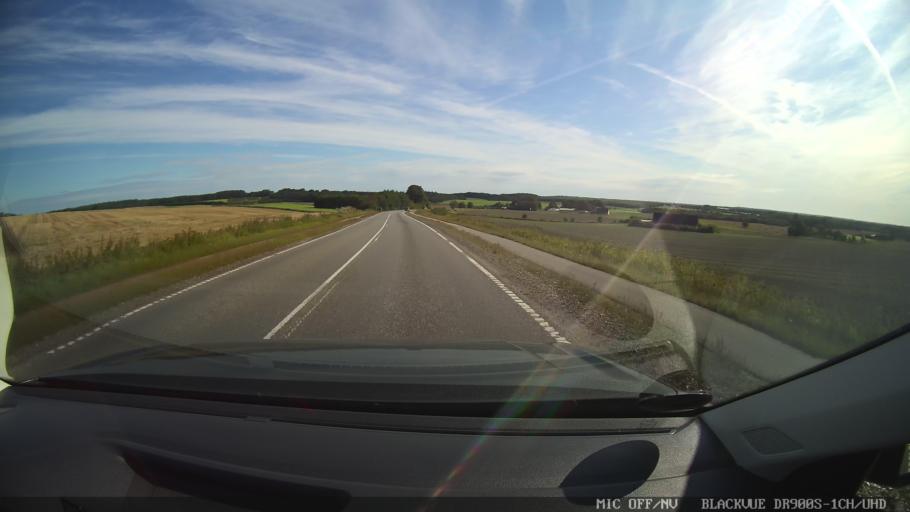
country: DK
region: North Denmark
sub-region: Mariagerfjord Kommune
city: Arden
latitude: 56.7726
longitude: 9.8246
